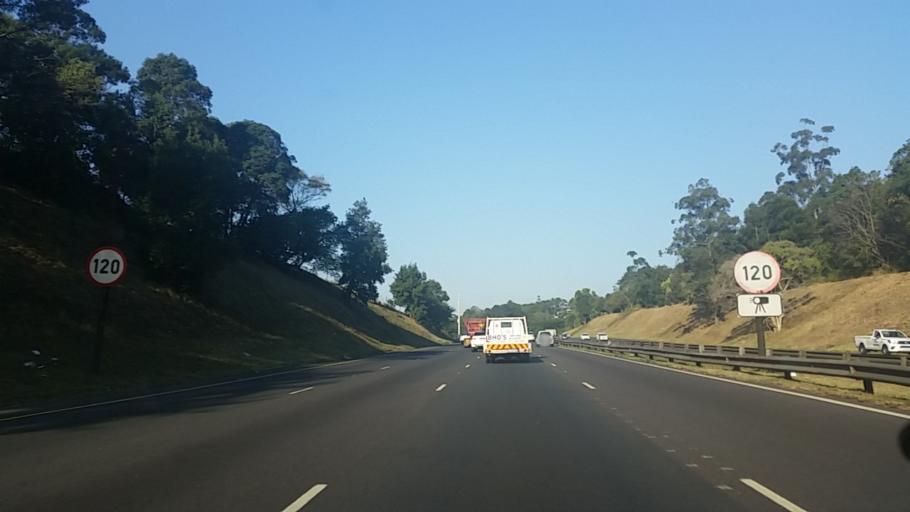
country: ZA
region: KwaZulu-Natal
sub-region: eThekwini Metropolitan Municipality
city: Berea
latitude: -29.8352
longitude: 30.8975
